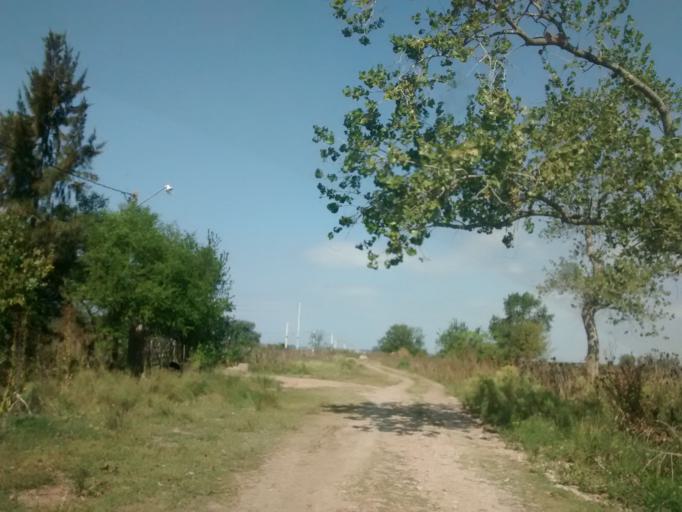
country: AR
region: Buenos Aires
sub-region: Partido de La Plata
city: La Plata
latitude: -35.0095
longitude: -57.9087
